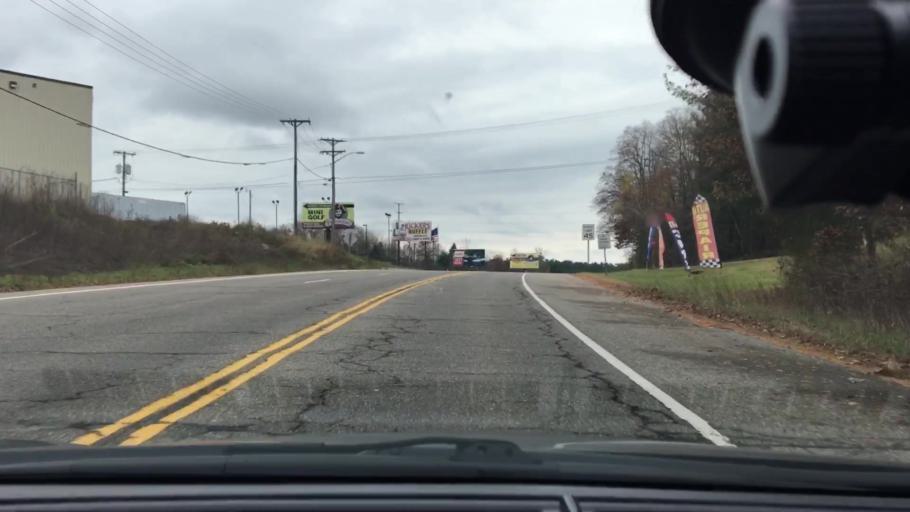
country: US
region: Wisconsin
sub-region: Columbia County
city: Wisconsin Dells
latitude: 43.6307
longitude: -89.7882
